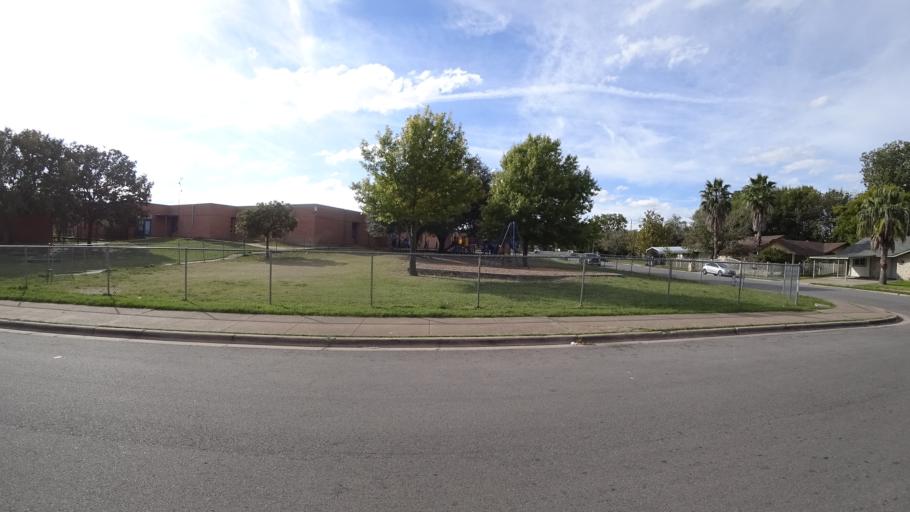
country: US
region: Texas
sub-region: Travis County
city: Onion Creek
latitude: 30.1978
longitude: -97.7538
